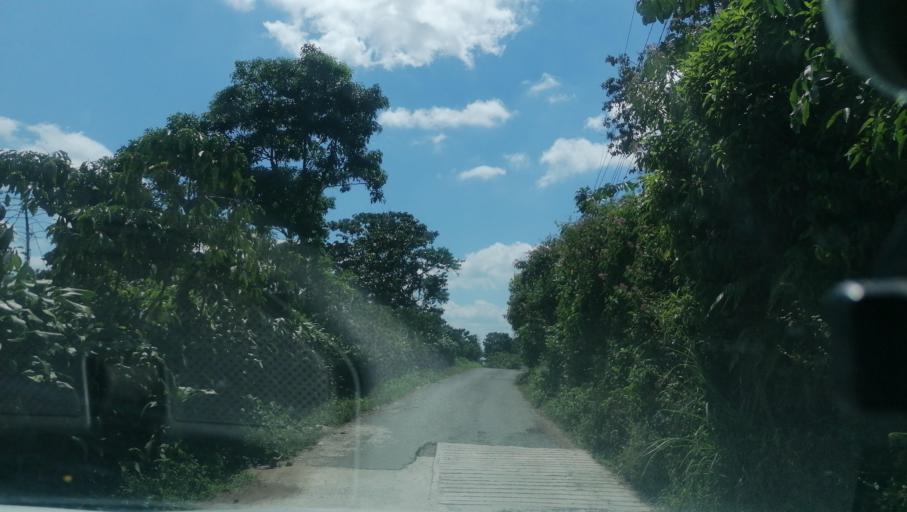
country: MX
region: Chiapas
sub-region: Cacahoatan
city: Benito Juarez
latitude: 15.0621
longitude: -92.1449
